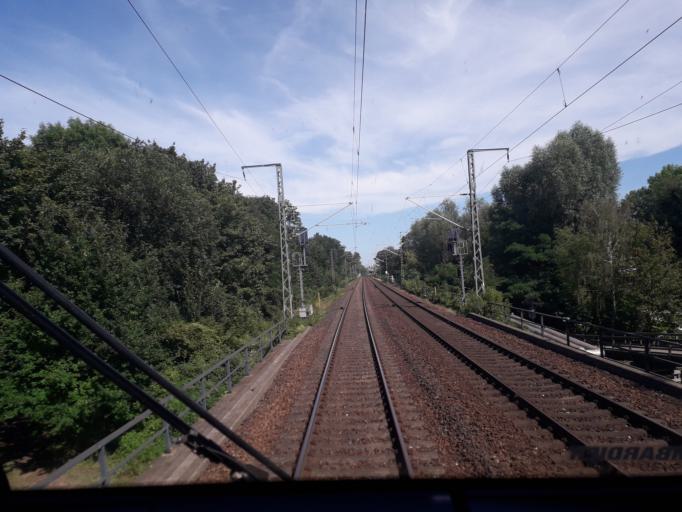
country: DE
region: Brandenburg
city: Potsdam
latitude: 52.3929
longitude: 13.0488
